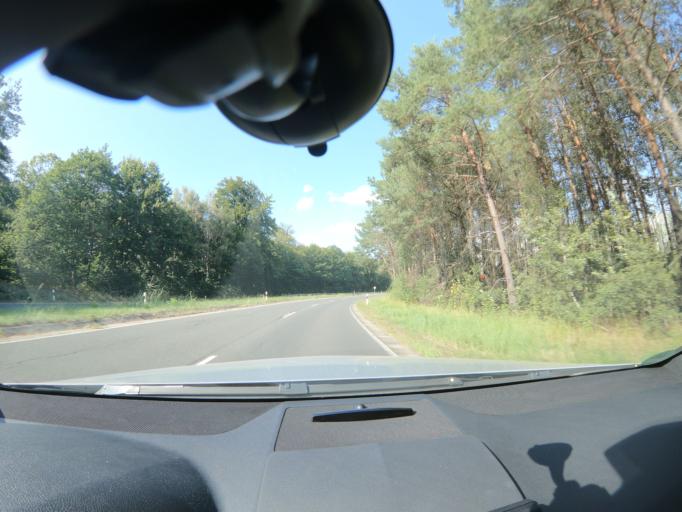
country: DE
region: Hesse
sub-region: Regierungsbezirk Giessen
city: Marburg an der Lahn
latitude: 50.8096
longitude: 8.8047
